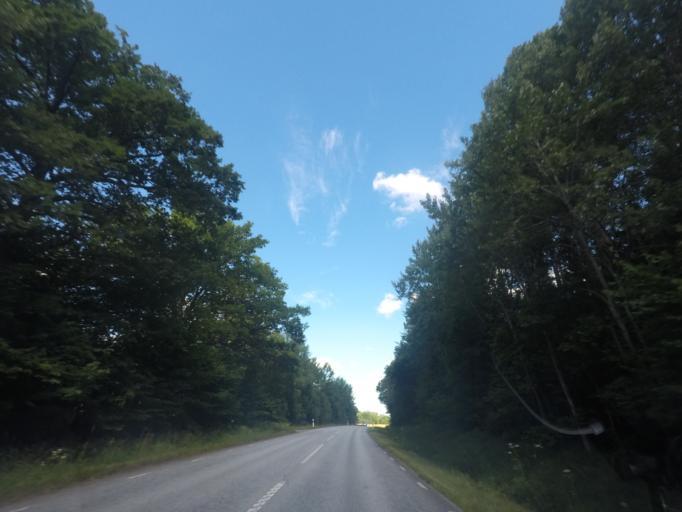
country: SE
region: Stockholm
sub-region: Norrtalje Kommun
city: Hallstavik
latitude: 59.9253
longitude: 18.7093
